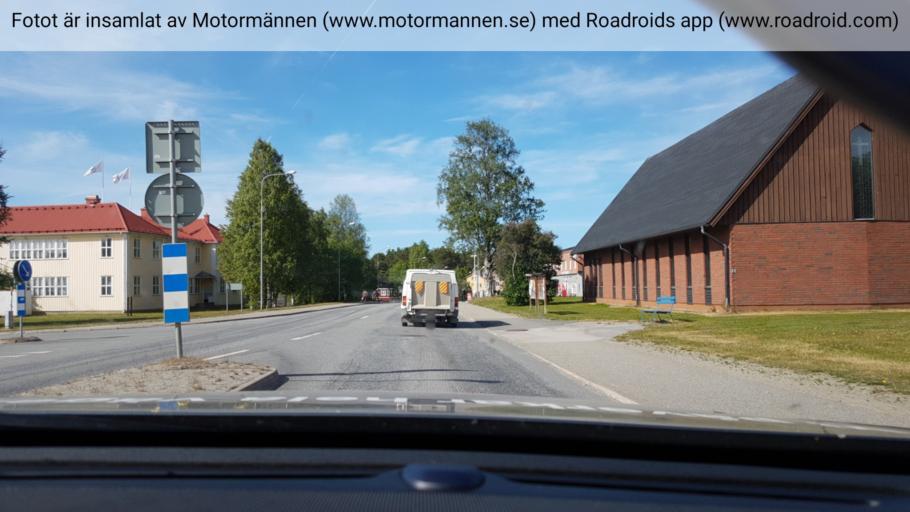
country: SE
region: Vaesterbotten
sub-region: Dorotea Kommun
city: Dorotea
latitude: 64.2609
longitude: 16.4085
